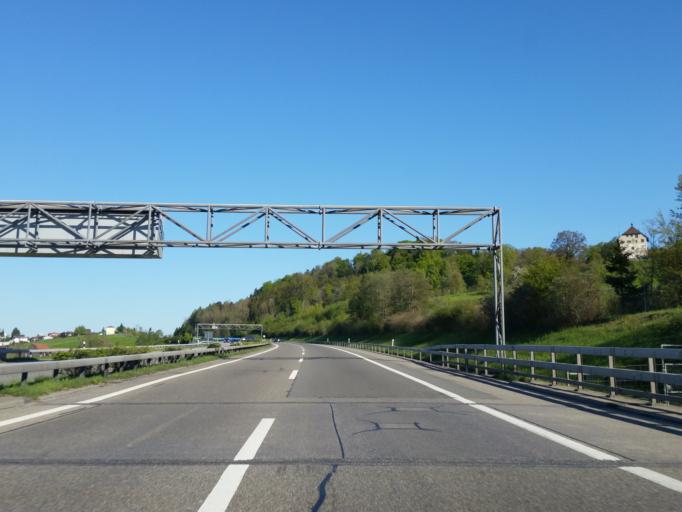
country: CH
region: Appenzell Ausserrhoden
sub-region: Bezirk Hinterland
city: Herisau
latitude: 47.4109
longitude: 9.2885
